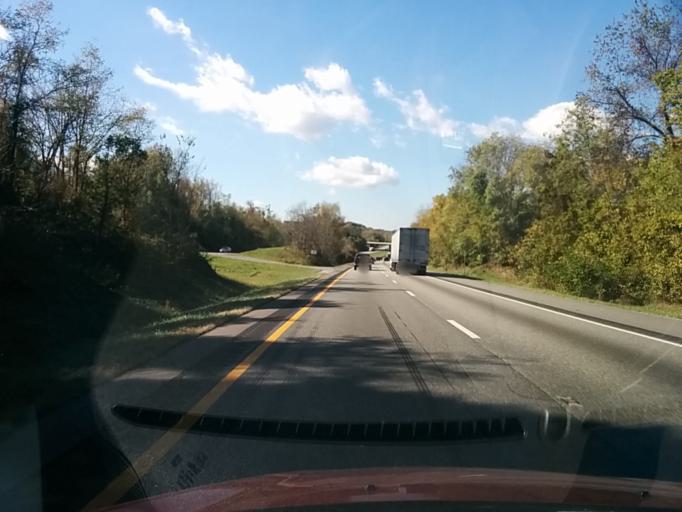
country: US
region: Virginia
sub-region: Botetourt County
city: Fincastle
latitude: 37.4815
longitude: -79.7814
